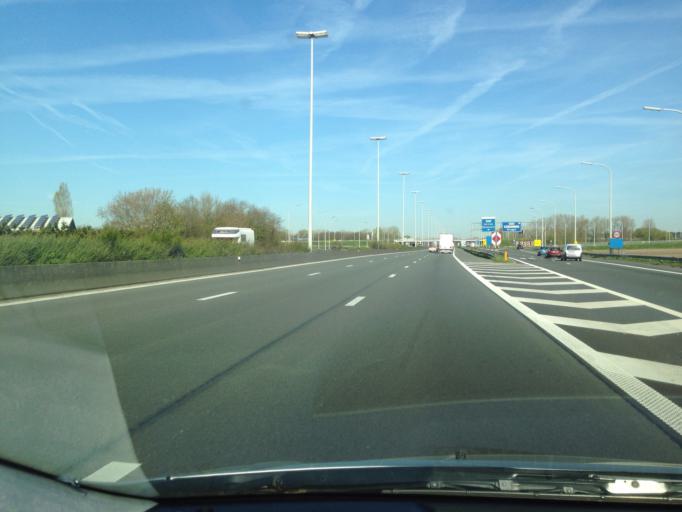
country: BE
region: Flanders
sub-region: Provincie West-Vlaanderen
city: Oostkamp
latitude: 51.1516
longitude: 3.2195
